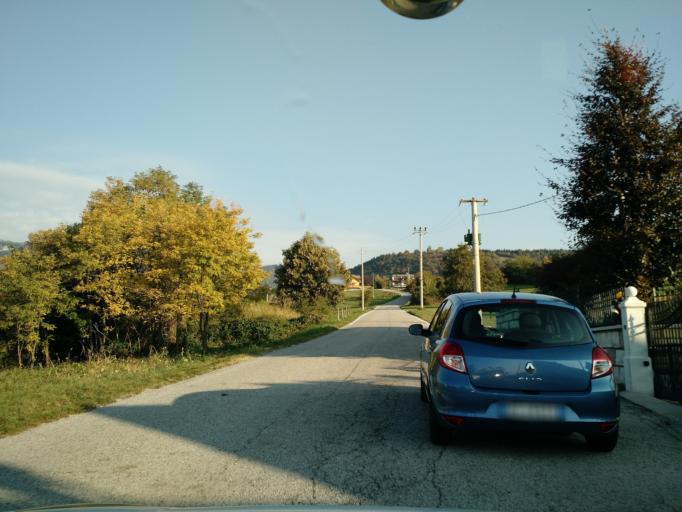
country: IT
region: Veneto
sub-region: Provincia di Vicenza
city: Lusiana
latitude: 45.7778
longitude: 11.5687
